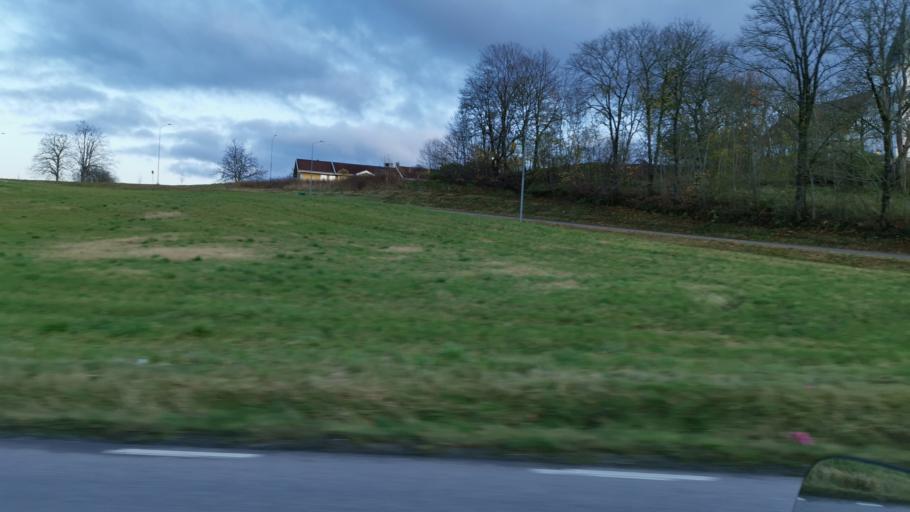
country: SE
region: Vaestra Goetaland
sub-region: Munkedals Kommun
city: Munkedal
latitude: 58.4683
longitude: 11.6593
